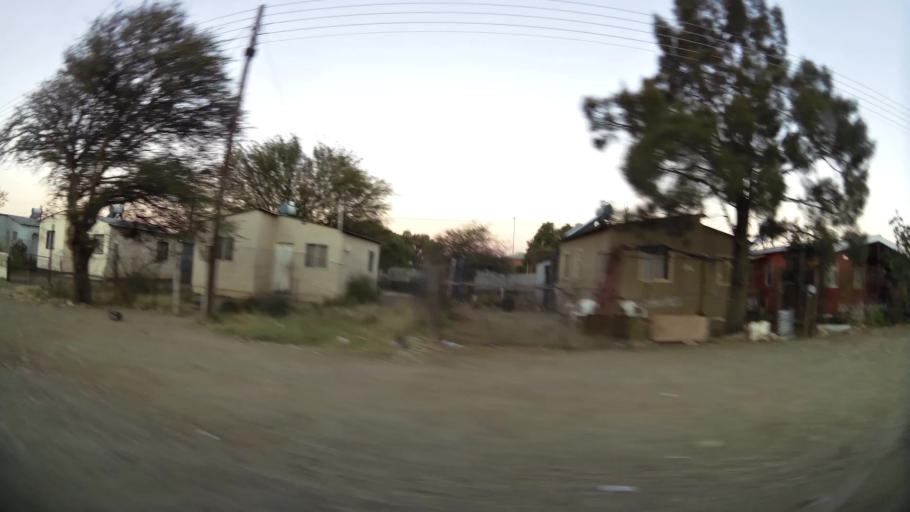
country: ZA
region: Northern Cape
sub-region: Frances Baard District Municipality
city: Kimberley
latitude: -28.7156
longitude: 24.7679
